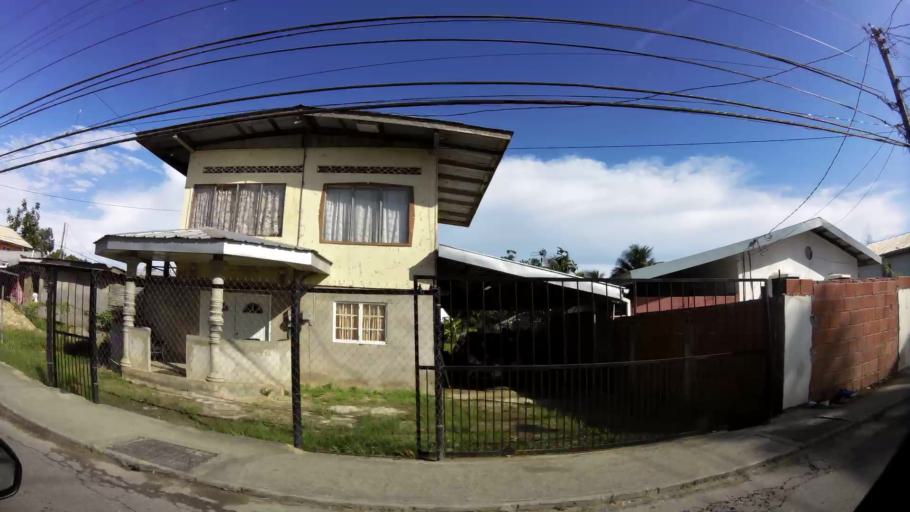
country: TT
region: Chaguanas
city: Chaguanas
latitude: 10.5262
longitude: -61.3910
